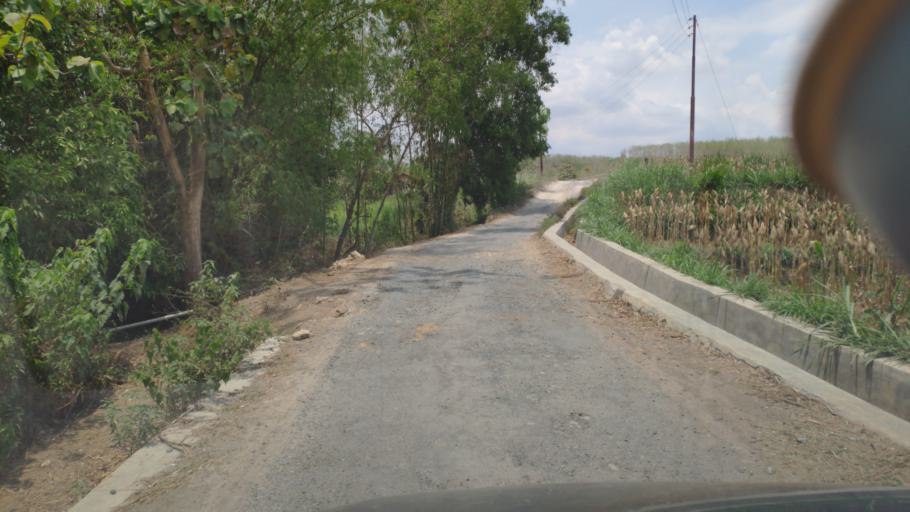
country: ID
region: Central Java
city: Ngapus
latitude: -6.9713
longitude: 111.2053
